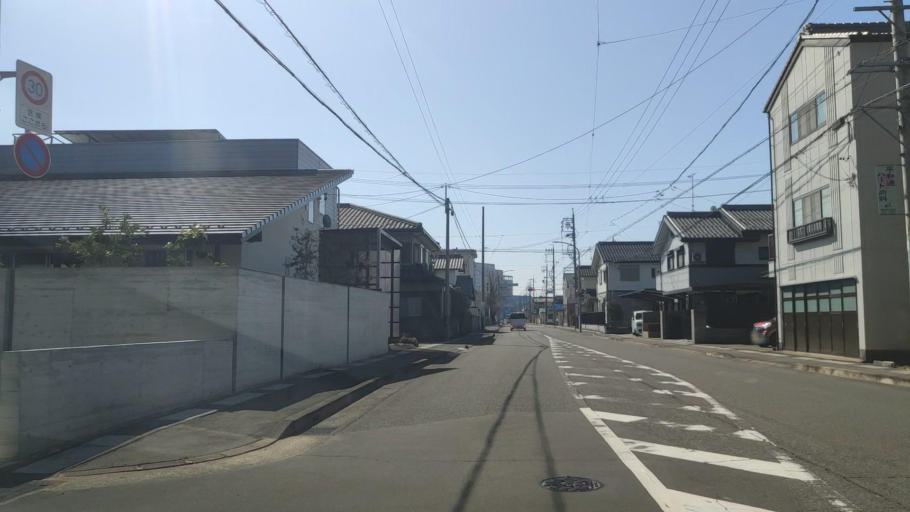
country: JP
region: Gifu
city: Gifu-shi
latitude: 35.4465
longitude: 136.7691
